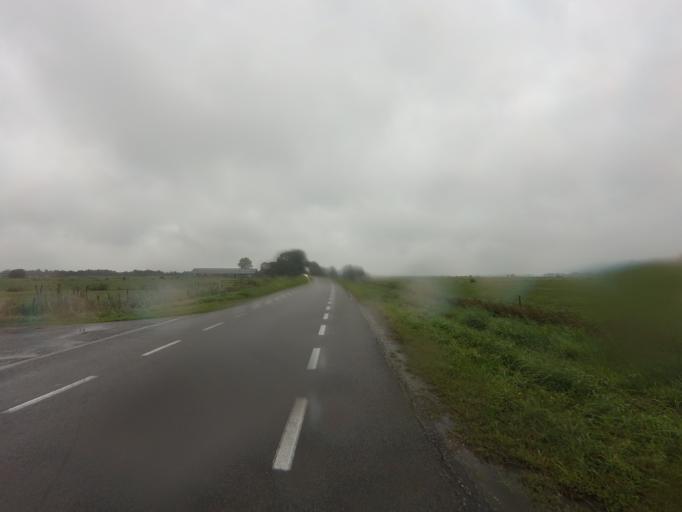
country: NL
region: Friesland
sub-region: Gemeente Smallingerland
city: Oudega
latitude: 53.0965
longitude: 5.9617
